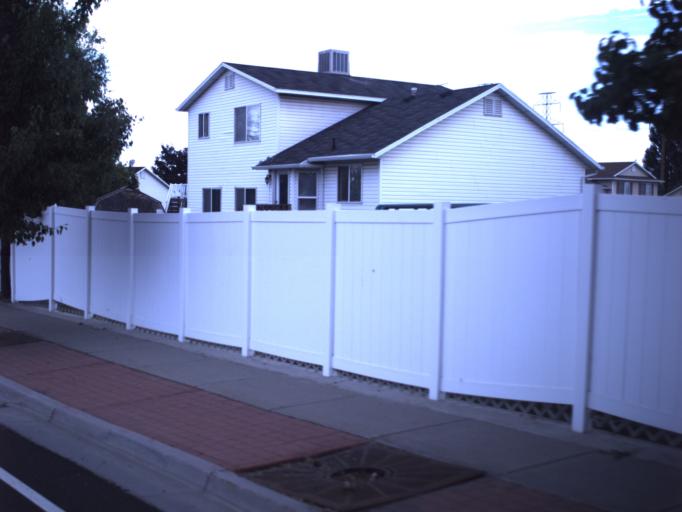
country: US
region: Utah
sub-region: Davis County
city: Clinton
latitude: 41.1617
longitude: -112.0559
